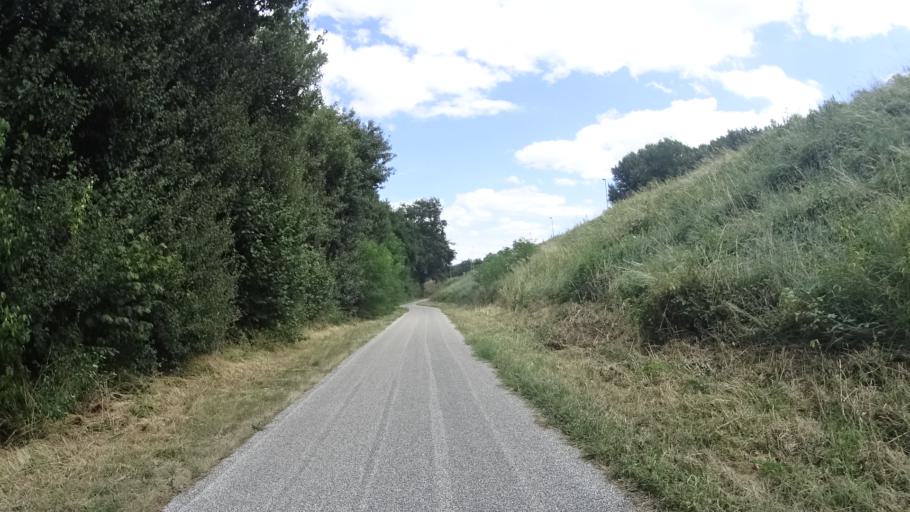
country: FR
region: Centre
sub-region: Departement d'Indre-et-Loire
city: La Ville-aux-Dames
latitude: 47.4036
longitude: 0.7675
